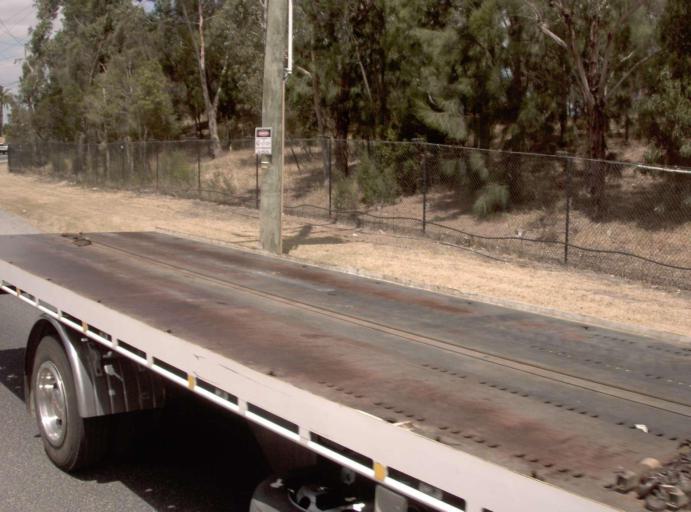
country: AU
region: Victoria
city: Heatherton
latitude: -37.9630
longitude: 145.1050
